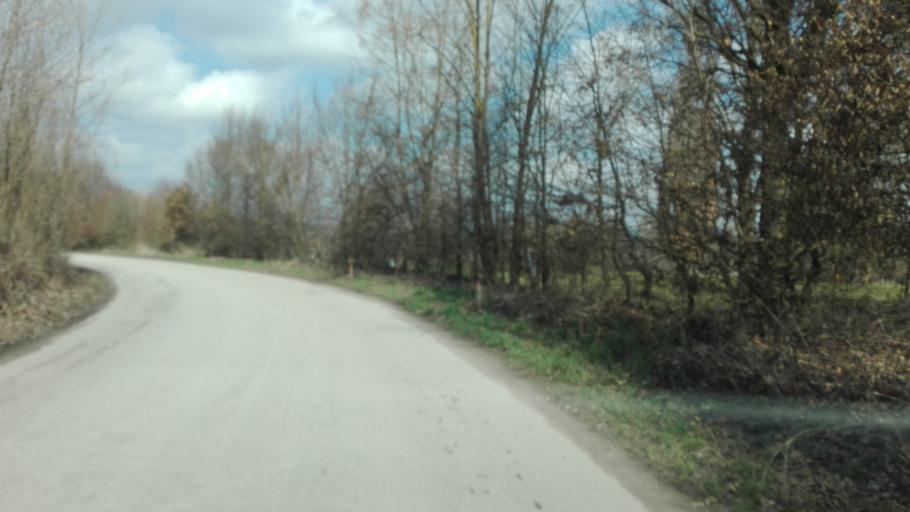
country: AT
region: Upper Austria
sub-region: Politischer Bezirk Urfahr-Umgebung
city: Feldkirchen an der Donau
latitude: 48.3299
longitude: 14.0654
